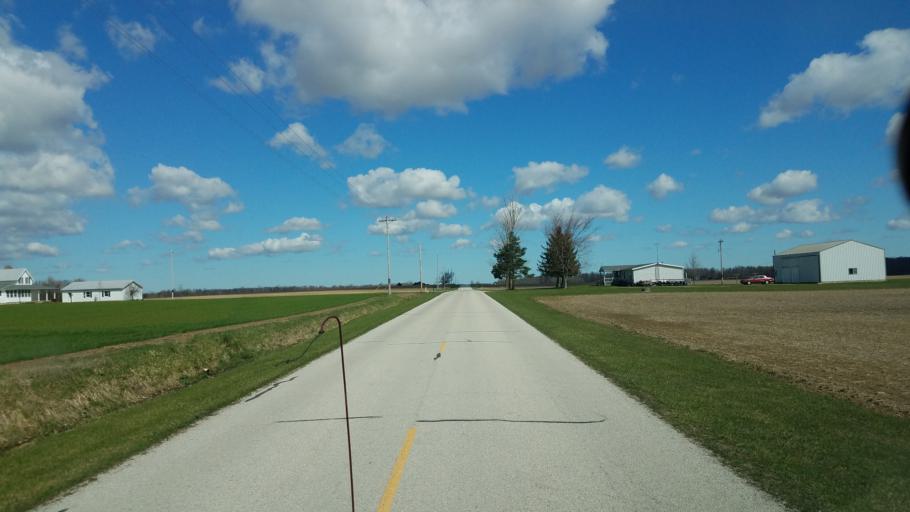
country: US
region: Ohio
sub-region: Sandusky County
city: Mount Carmel
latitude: 41.1377
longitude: -82.9383
